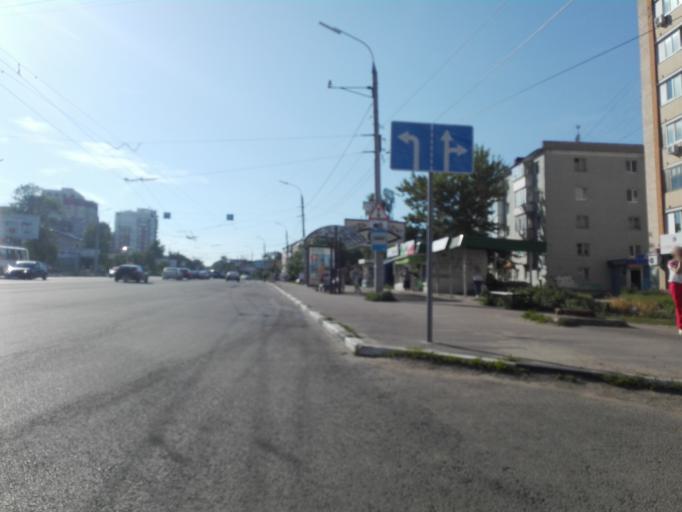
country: RU
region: Orjol
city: Orel
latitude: 52.9786
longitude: 36.0774
